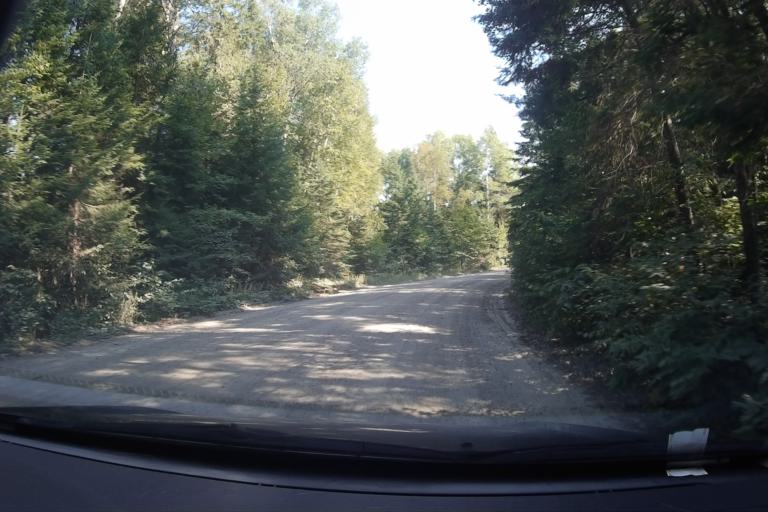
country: CA
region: Ontario
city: Huntsville
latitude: 45.5745
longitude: -78.7098
